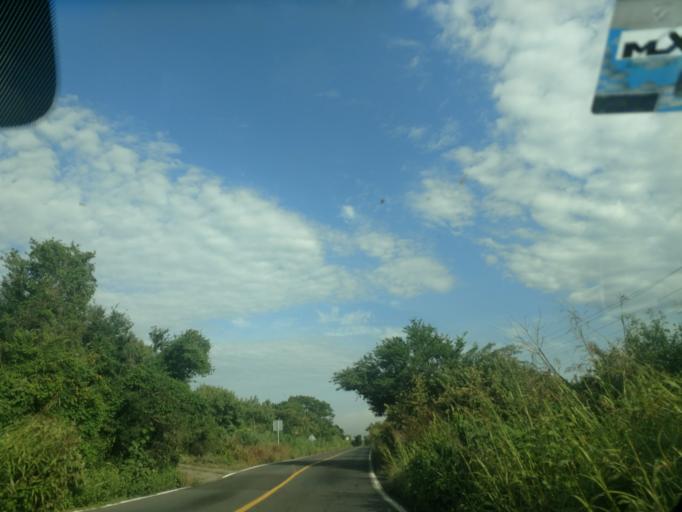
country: MX
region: Jalisco
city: Ameca
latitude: 20.5204
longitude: -104.1204
